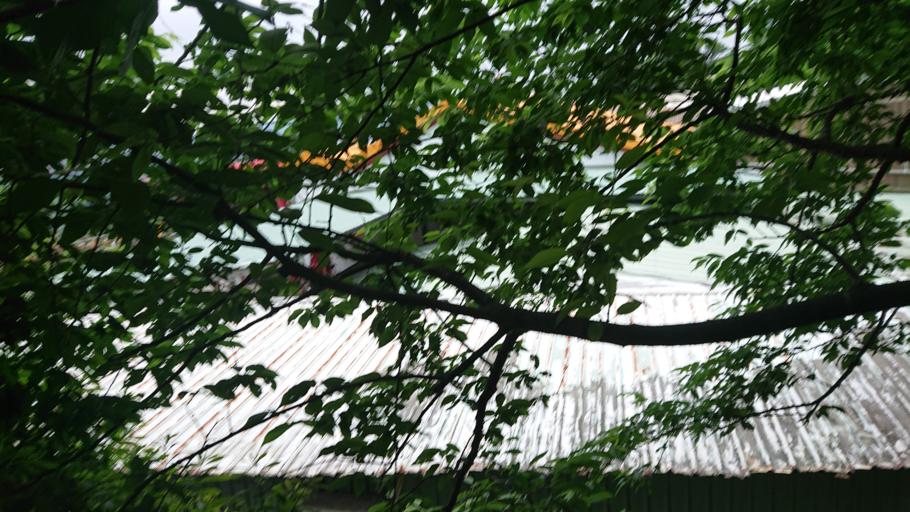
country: TW
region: Taiwan
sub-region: Taoyuan
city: Taoyuan
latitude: 24.9296
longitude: 121.3449
